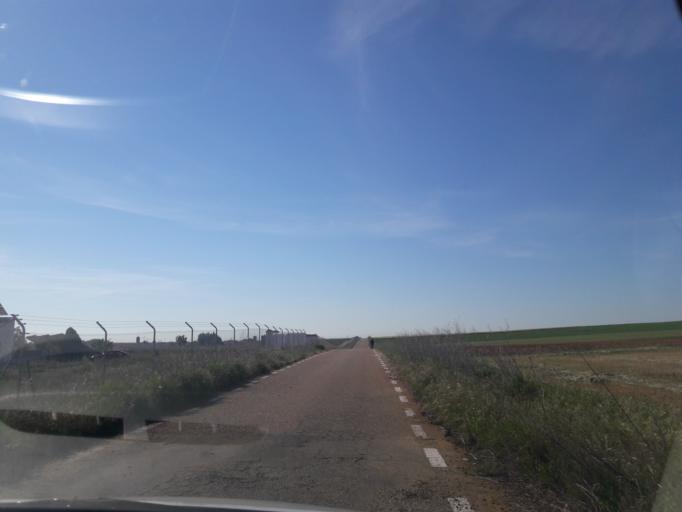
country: ES
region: Castille and Leon
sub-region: Provincia de Salamanca
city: Parada de Rubiales
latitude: 41.1558
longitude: -5.4488
